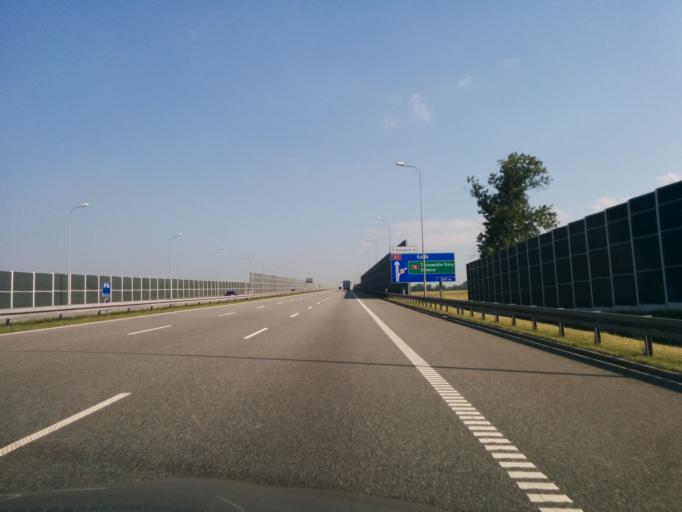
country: PL
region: Silesian Voivodeship
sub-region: Powiat tarnogorski
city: Wieszowa
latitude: 50.3372
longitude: 18.7282
